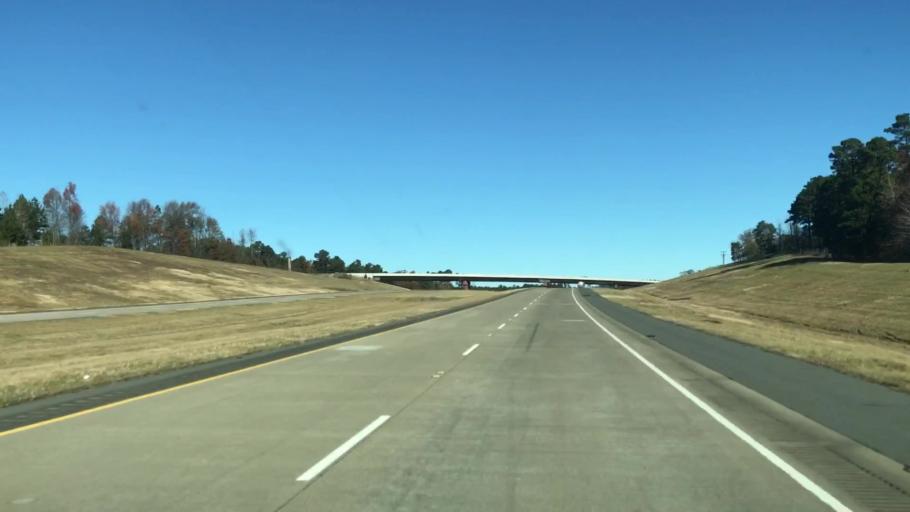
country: US
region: Louisiana
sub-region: Caddo Parish
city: Vivian
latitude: 32.9748
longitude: -93.9085
